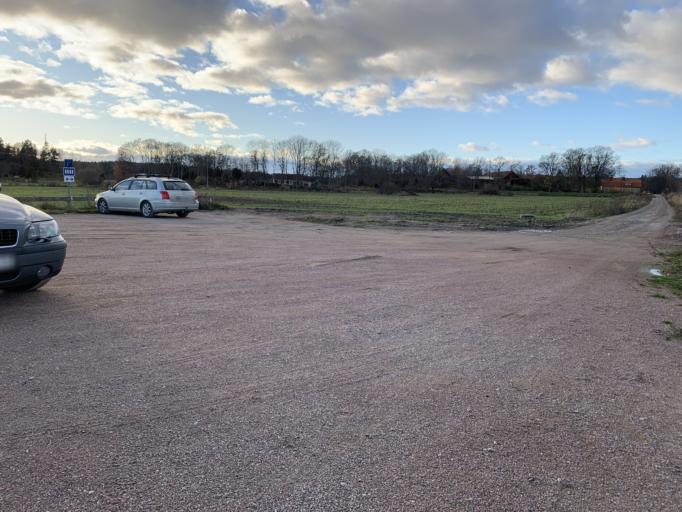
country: SE
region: Soedermanland
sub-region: Eskilstuna Kommun
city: Torshalla
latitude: 59.5240
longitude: 16.4455
